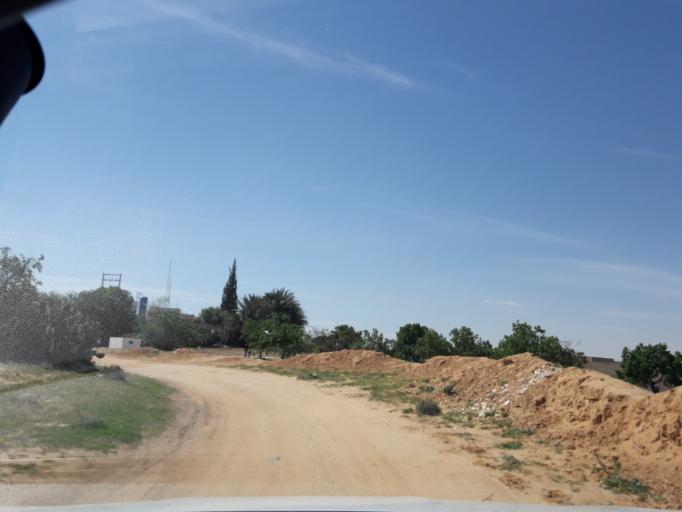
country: TN
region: Safaqis
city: Sfax
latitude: 34.7459
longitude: 10.5109
